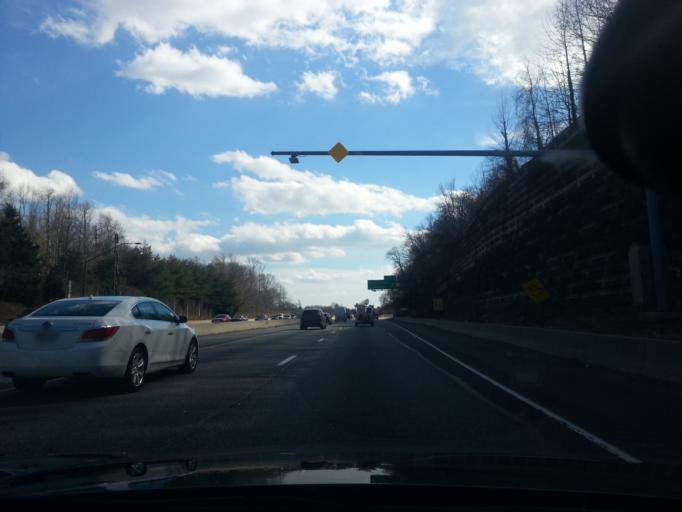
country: US
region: Pennsylvania
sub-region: Delaware County
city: Swarthmore
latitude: 39.9185
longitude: -75.3625
